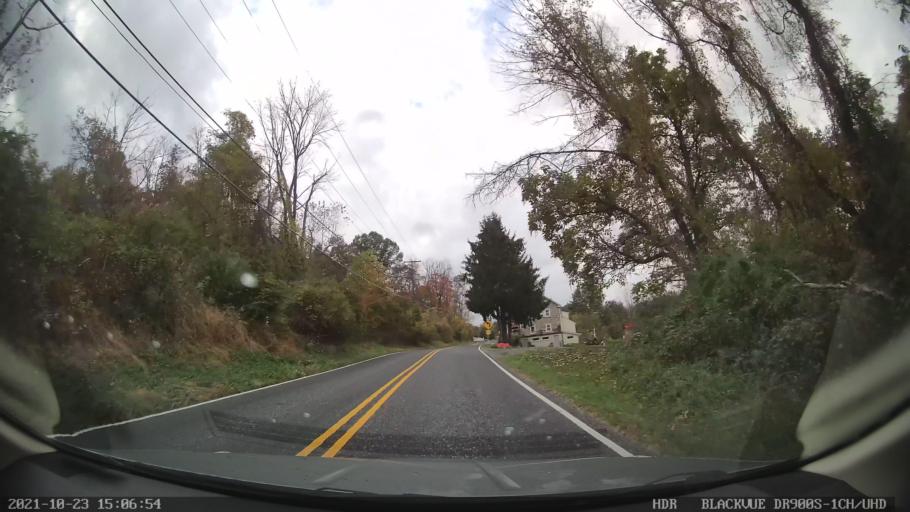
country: US
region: Pennsylvania
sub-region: Berks County
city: Bally
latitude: 40.4358
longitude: -75.5966
